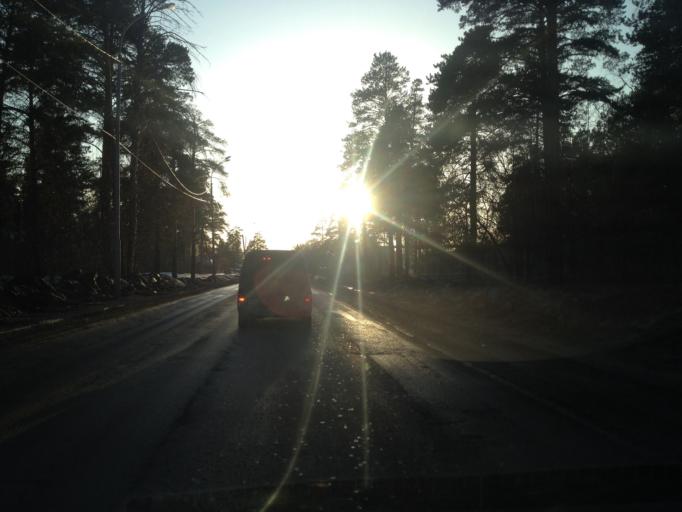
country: RU
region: Sverdlovsk
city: Sovkhoznyy
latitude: 56.7630
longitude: 60.5798
